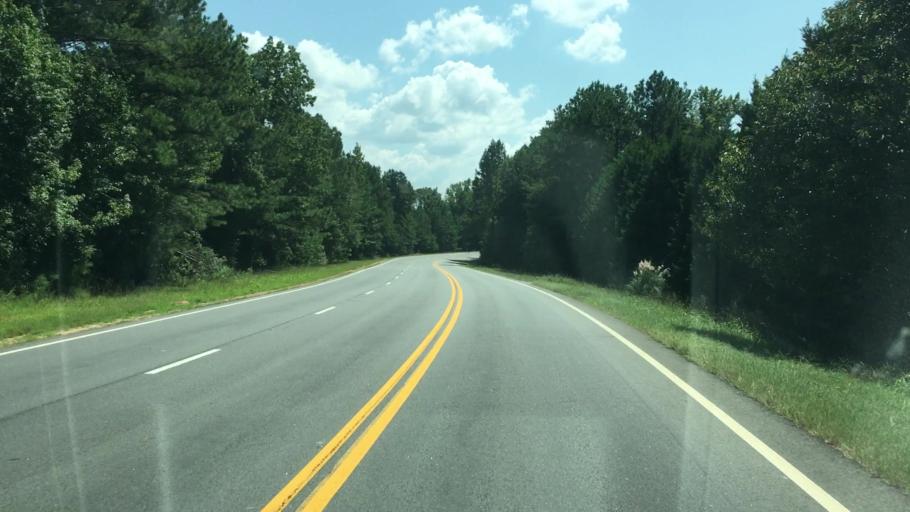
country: US
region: Georgia
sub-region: Morgan County
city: Madison
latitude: 33.7246
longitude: -83.4316
